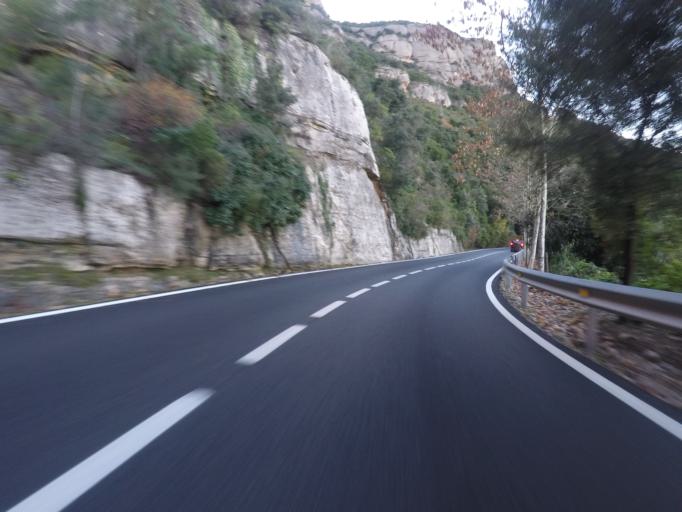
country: ES
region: Catalonia
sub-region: Provincia de Barcelona
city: Monistrol de Montserrat
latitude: 41.6035
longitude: 1.8262
